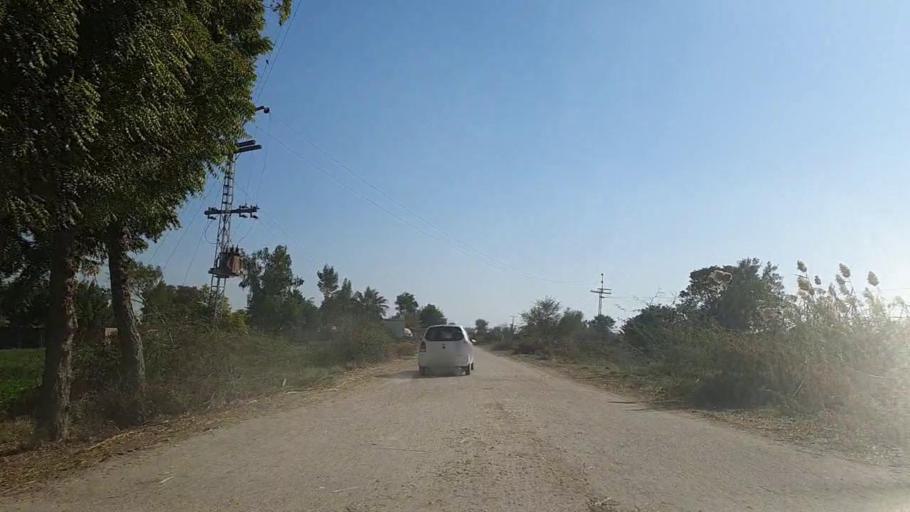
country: PK
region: Sindh
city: Nawabshah
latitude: 26.2281
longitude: 68.4280
